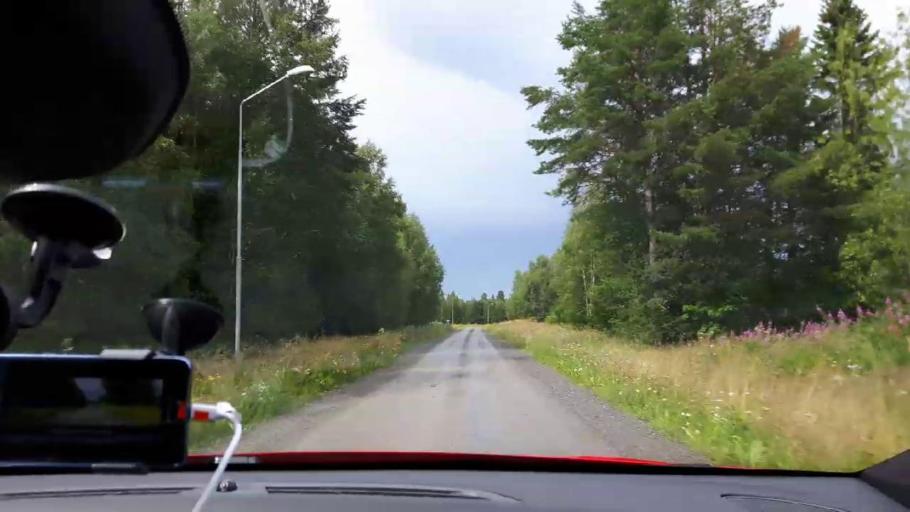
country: SE
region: Jaemtland
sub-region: Stroemsunds Kommun
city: Stroemsund
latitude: 64.0565
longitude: 15.8915
